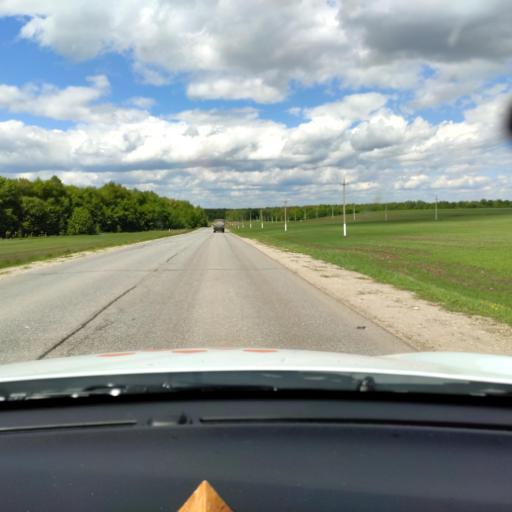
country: RU
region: Tatarstan
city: Verkhniy Uslon
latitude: 55.5751
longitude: 48.8977
